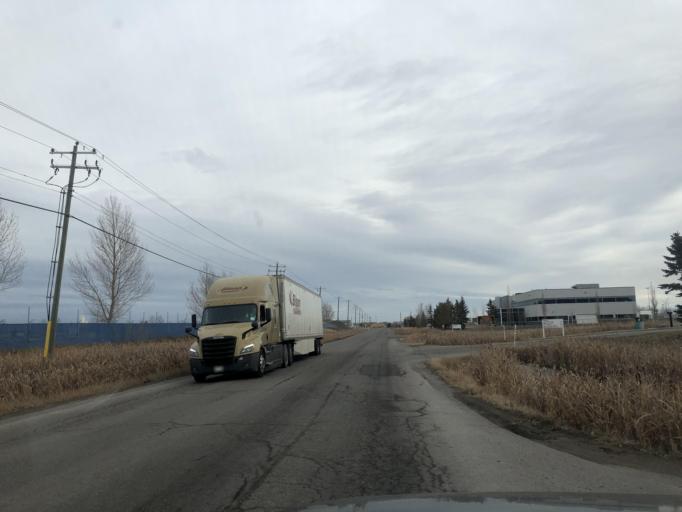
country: CA
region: Alberta
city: Chestermere
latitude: 50.9833
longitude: -113.9101
